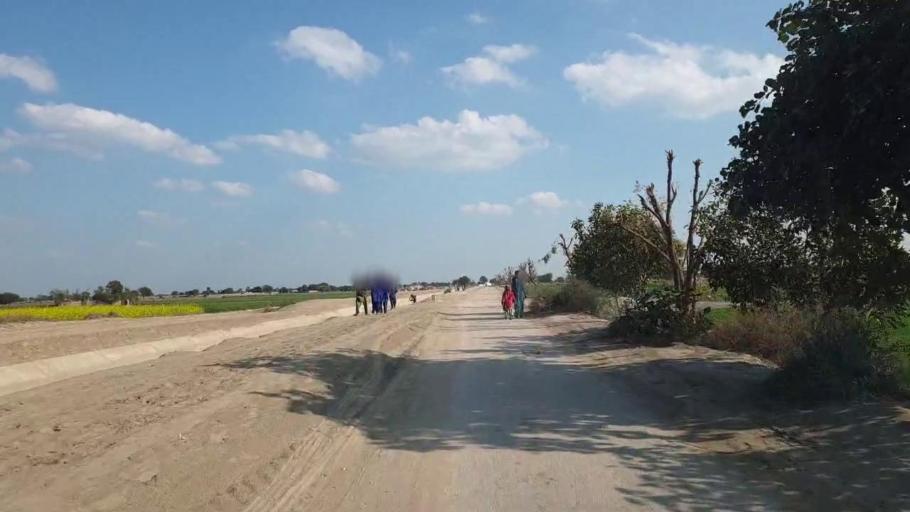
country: PK
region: Sindh
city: Shahpur Chakar
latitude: 26.1081
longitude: 68.5741
